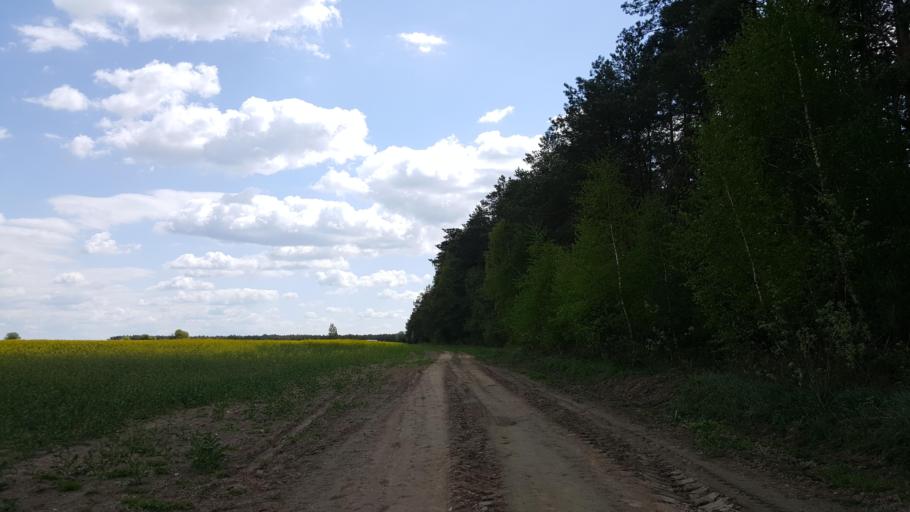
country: BY
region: Brest
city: Kamyanyets
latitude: 52.3878
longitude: 23.9387
